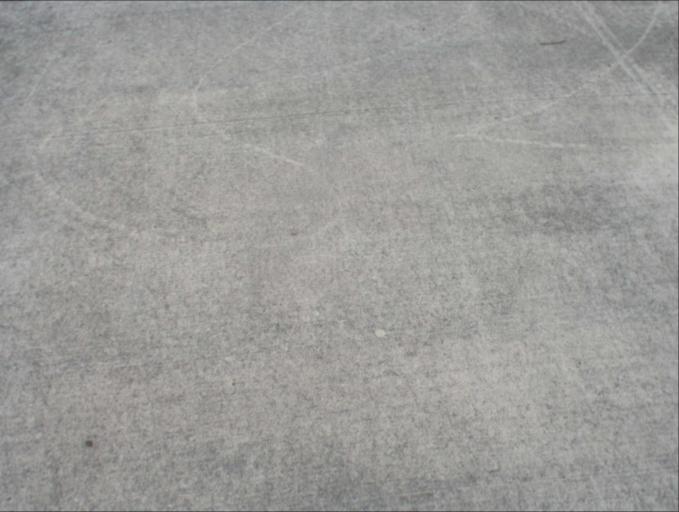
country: AU
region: Queensland
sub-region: Logan
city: Park Ridge South
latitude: -27.6988
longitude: 153.0387
